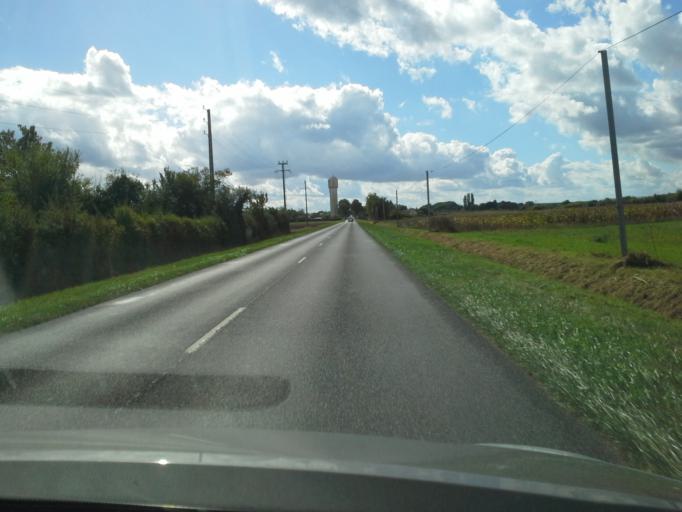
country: FR
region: Centre
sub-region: Departement du Loir-et-Cher
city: Pontlevoy
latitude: 47.4032
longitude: 1.2653
